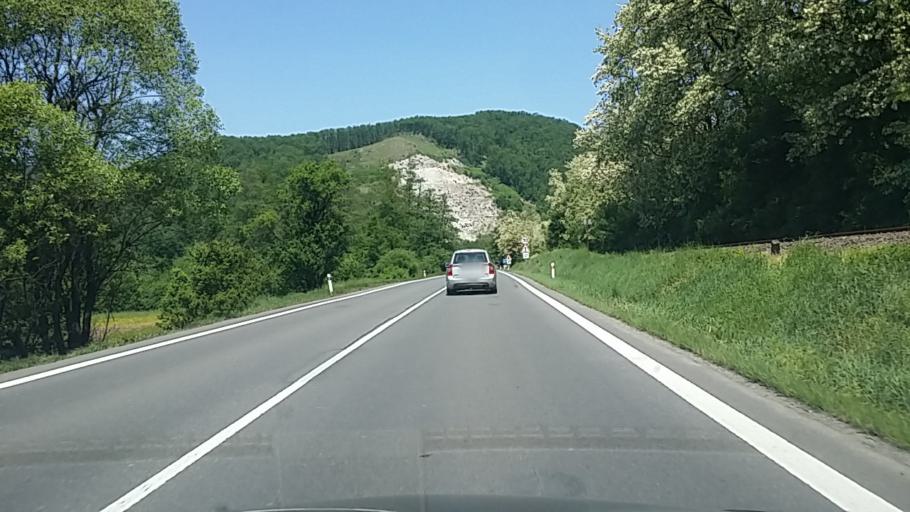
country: SK
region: Banskobystricky
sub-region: Okres Banska Bystrica
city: Zvolen
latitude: 48.5154
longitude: 19.0981
